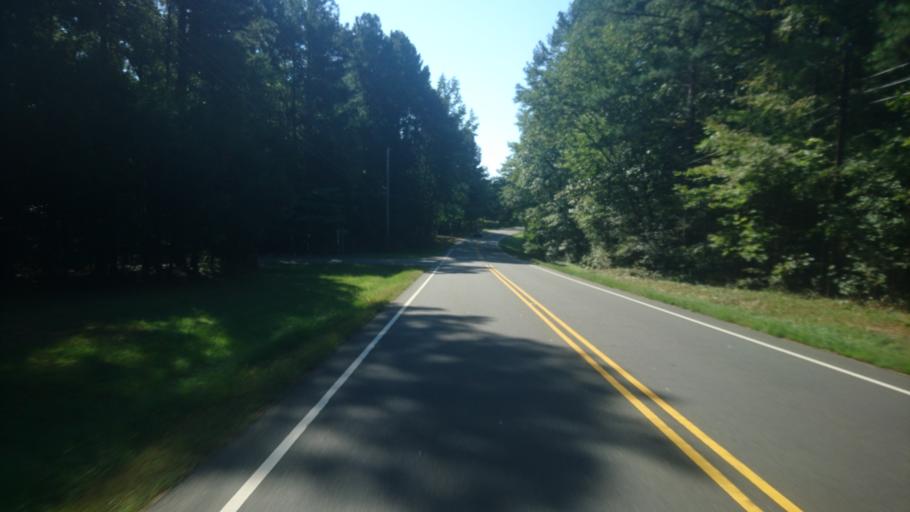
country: US
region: North Carolina
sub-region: Orange County
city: Hillsborough
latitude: 36.0077
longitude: -79.0668
